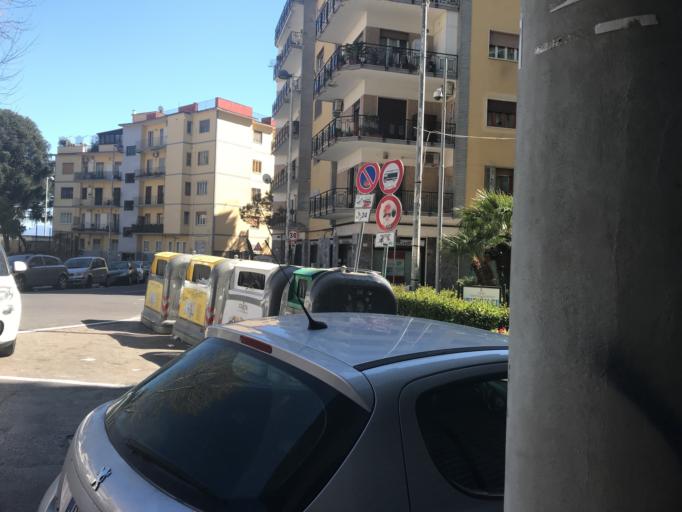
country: IT
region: Campania
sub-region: Provincia di Napoli
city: Napoli
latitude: 40.8605
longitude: 14.2216
